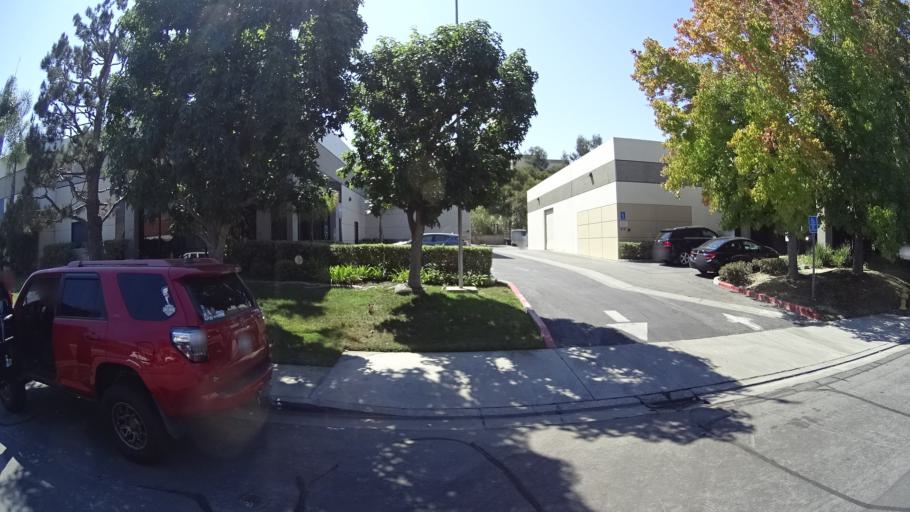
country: US
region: California
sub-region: Orange County
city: San Clemente
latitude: 33.4492
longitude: -117.5902
